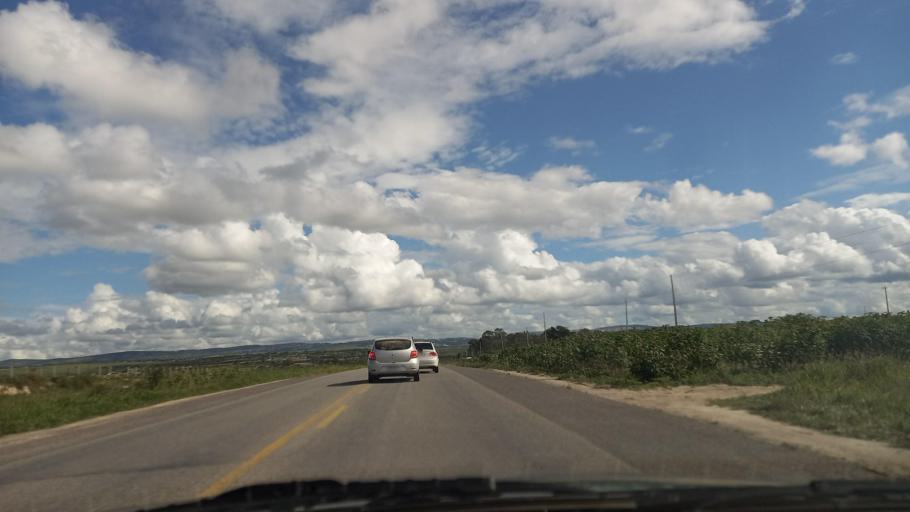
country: BR
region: Pernambuco
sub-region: Sao Joao
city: Sao Joao
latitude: -8.7862
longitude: -36.4325
